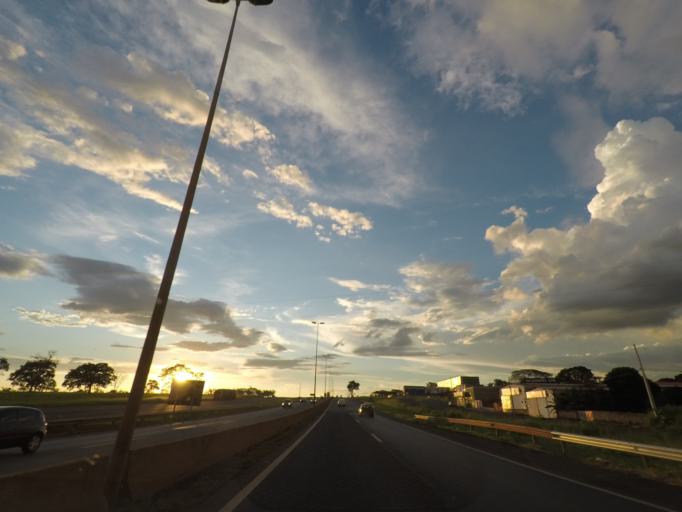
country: BR
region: Minas Gerais
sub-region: Uberaba
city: Uberaba
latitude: -19.7792
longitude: -47.9543
